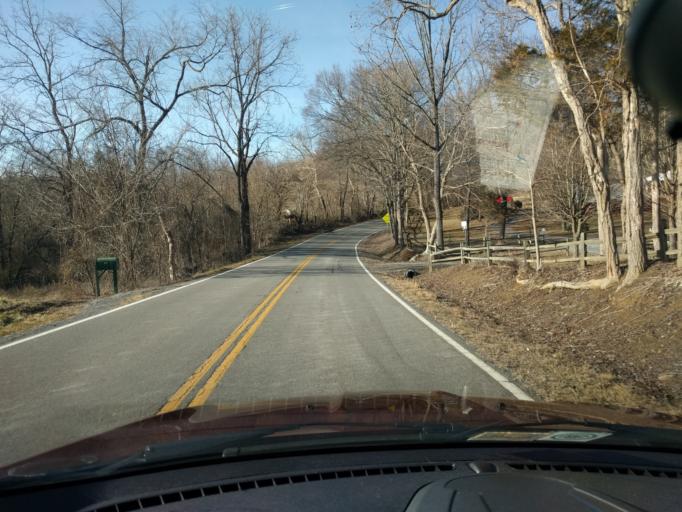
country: US
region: Virginia
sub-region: Botetourt County
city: Buchanan
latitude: 37.5586
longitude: -79.7261
